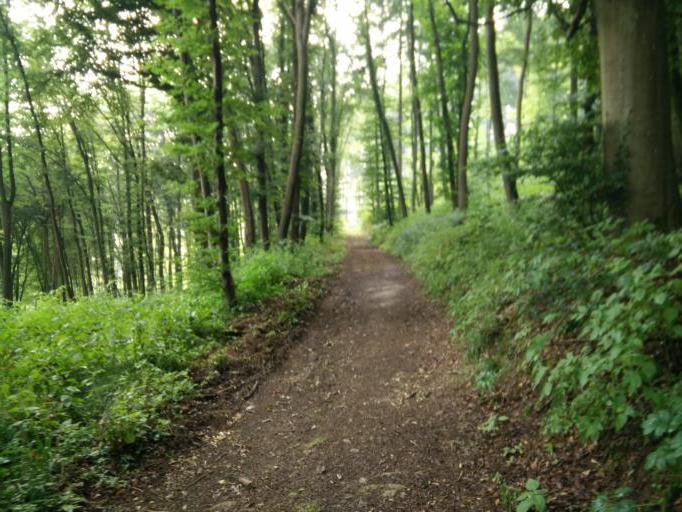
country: LU
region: Luxembourg
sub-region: Canton de Capellen
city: Mamer
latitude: 49.6408
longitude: 6.0437
